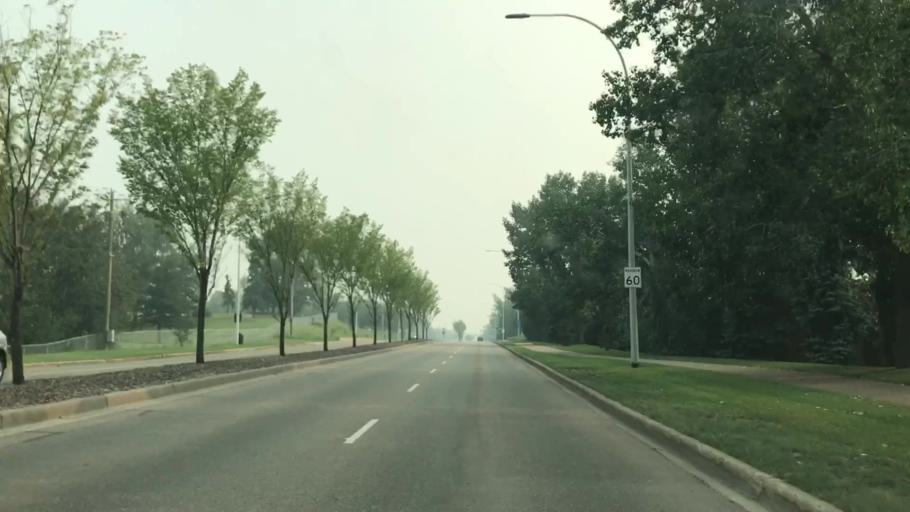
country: CA
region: Alberta
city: Sherwood Park
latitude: 53.5334
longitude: -113.3202
